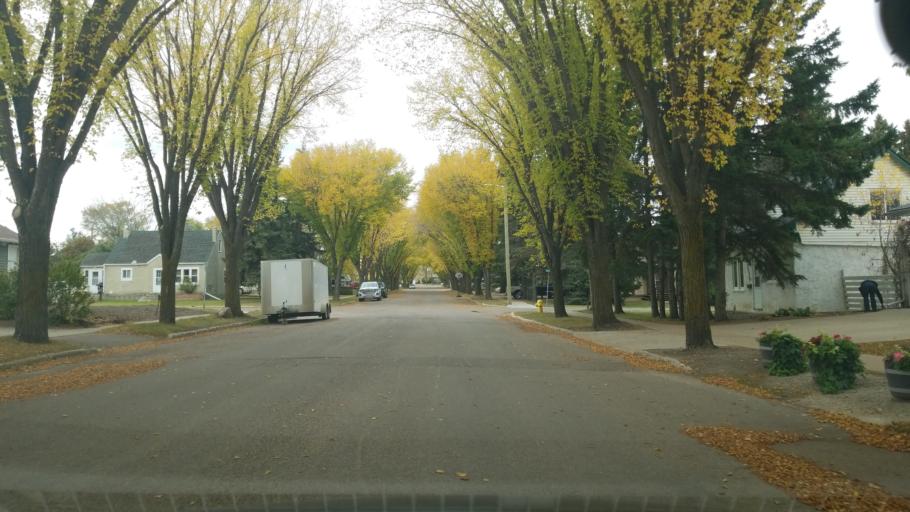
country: CA
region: Saskatchewan
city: Lloydminster
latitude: 53.2798
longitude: -110.0148
